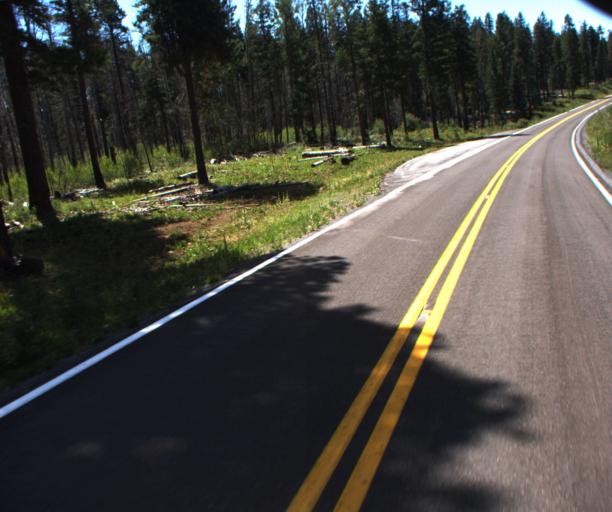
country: US
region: Arizona
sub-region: Apache County
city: Eagar
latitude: 33.6249
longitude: -109.3269
